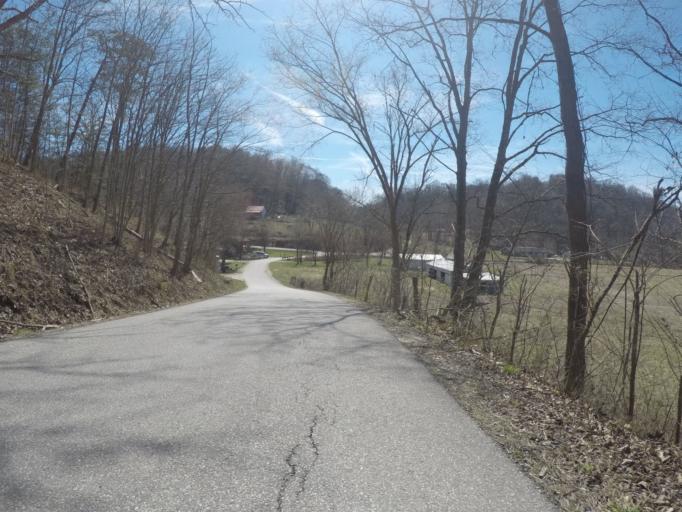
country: US
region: Ohio
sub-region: Lawrence County
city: South Point
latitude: 38.4671
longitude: -82.5691
